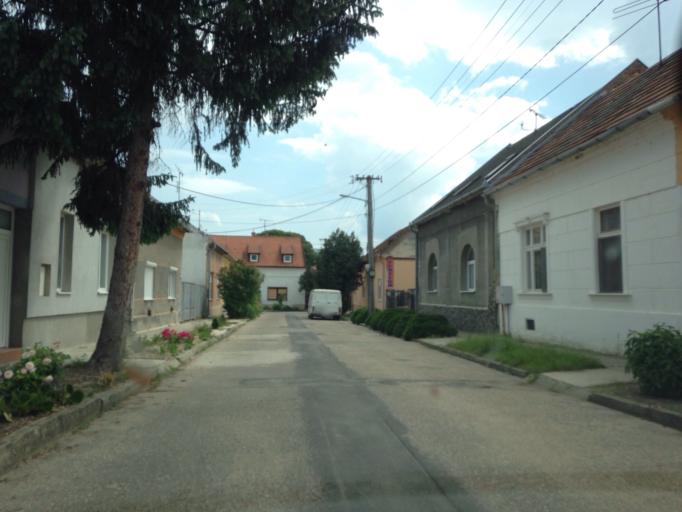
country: SK
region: Nitriansky
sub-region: Okres Nove Zamky
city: Sturovo
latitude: 47.7965
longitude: 18.7216
